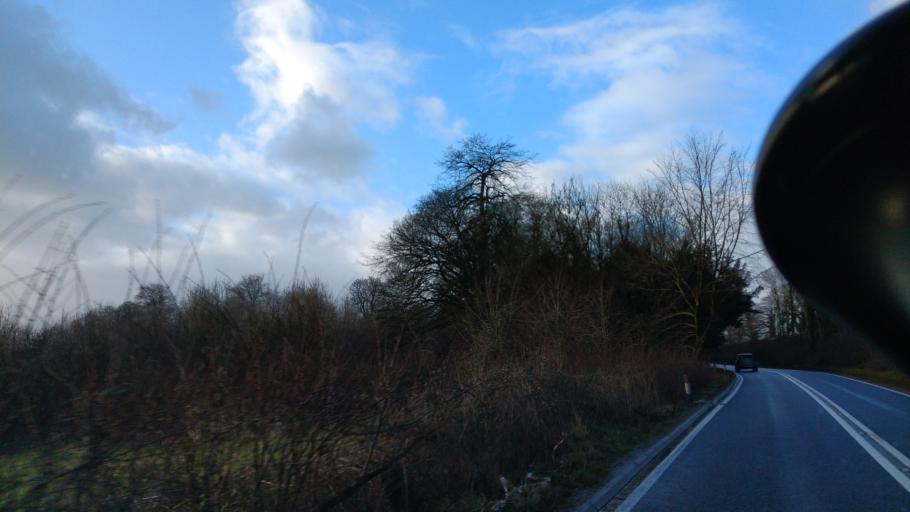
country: GB
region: England
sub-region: Somerset
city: Evercreech
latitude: 51.1956
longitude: -2.4526
